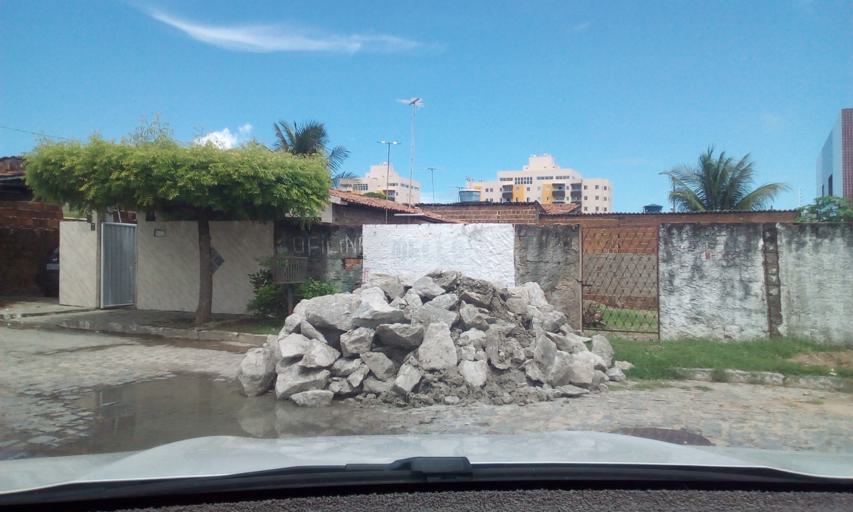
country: BR
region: Paraiba
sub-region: Cabedelo
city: Cabedelo
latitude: -6.9863
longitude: -34.8301
